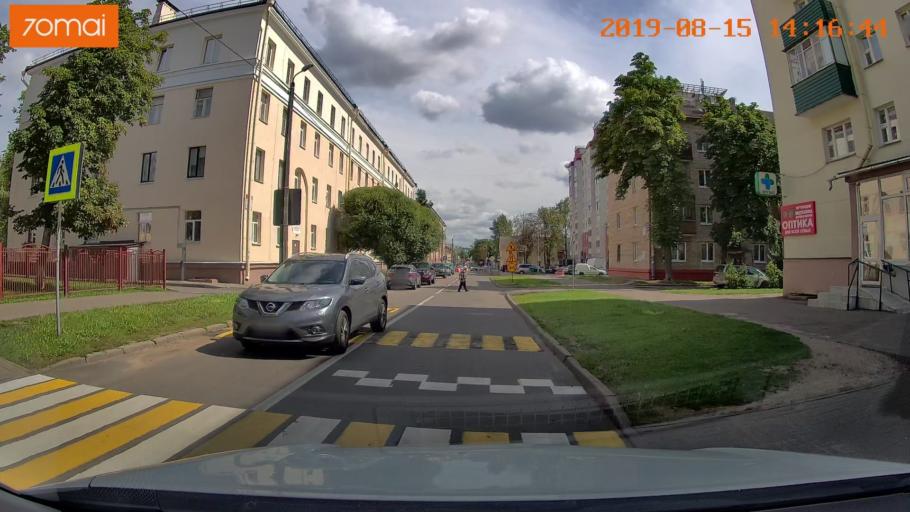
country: BY
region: Minsk
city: Minsk
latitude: 53.8853
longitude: 27.5926
